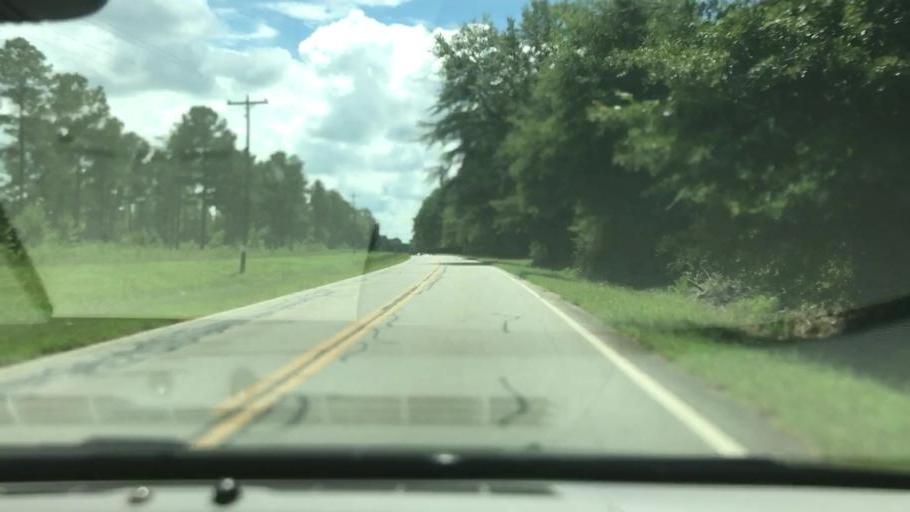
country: US
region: Georgia
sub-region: Quitman County
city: Georgetown
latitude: 32.1127
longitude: -85.0378
